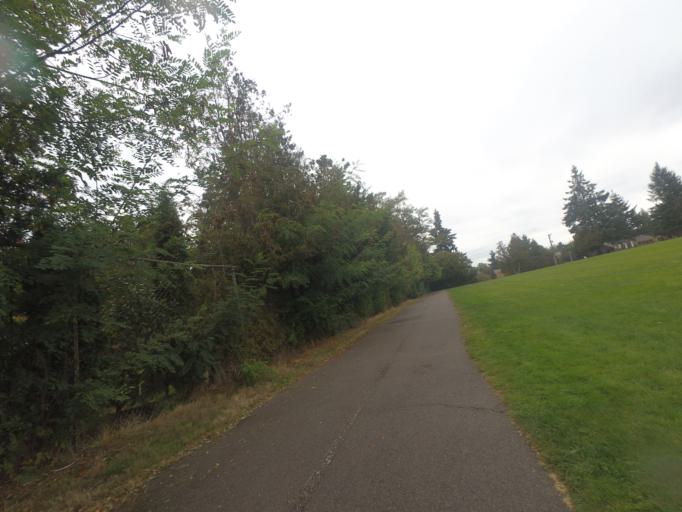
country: US
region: Washington
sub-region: Pierce County
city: University Place
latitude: 47.2198
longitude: -122.5423
